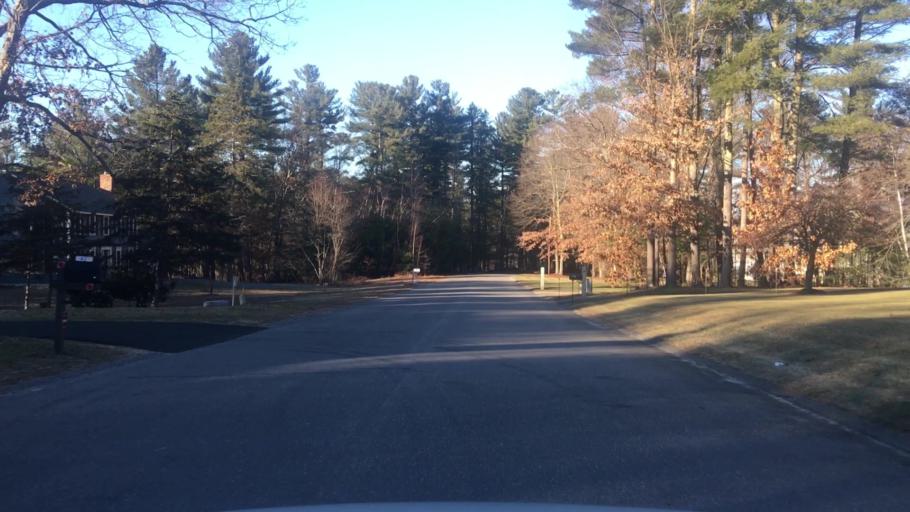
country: US
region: New Hampshire
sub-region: Rockingham County
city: Londonderry
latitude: 42.8770
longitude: -71.3780
